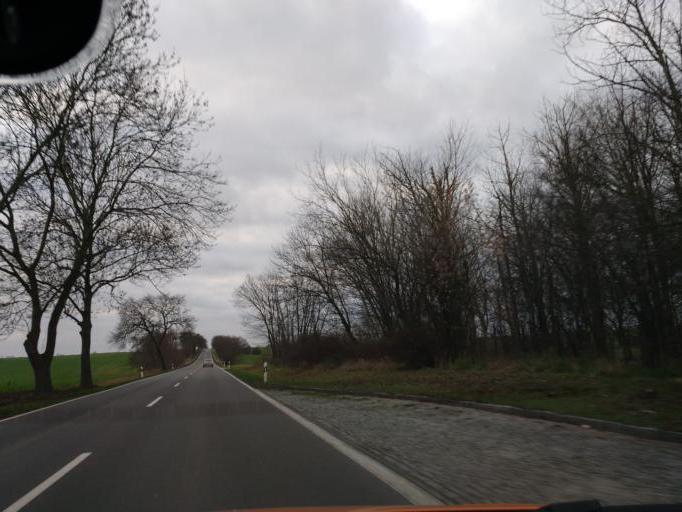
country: DE
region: Brandenburg
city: Wriezen
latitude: 52.7023
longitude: 14.1171
